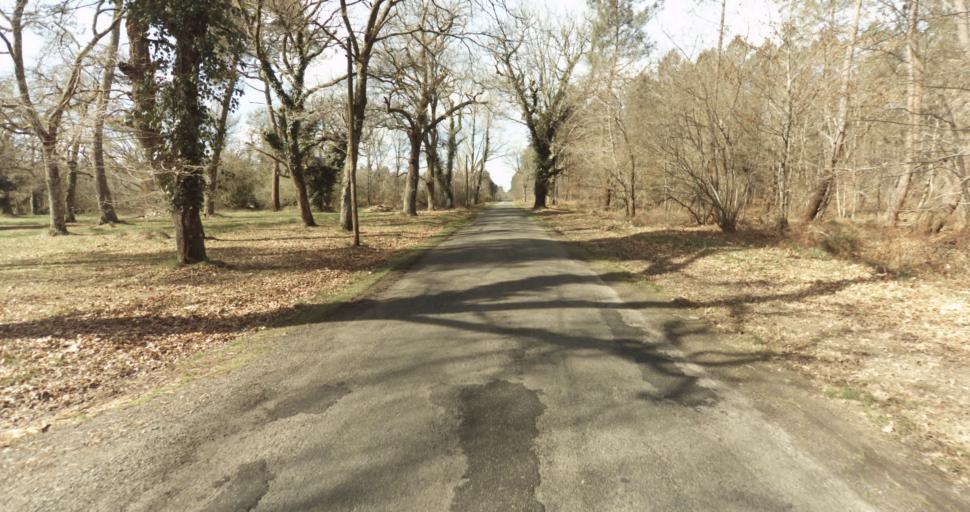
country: FR
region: Aquitaine
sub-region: Departement des Landes
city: Roquefort
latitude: 44.0659
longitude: -0.3284
